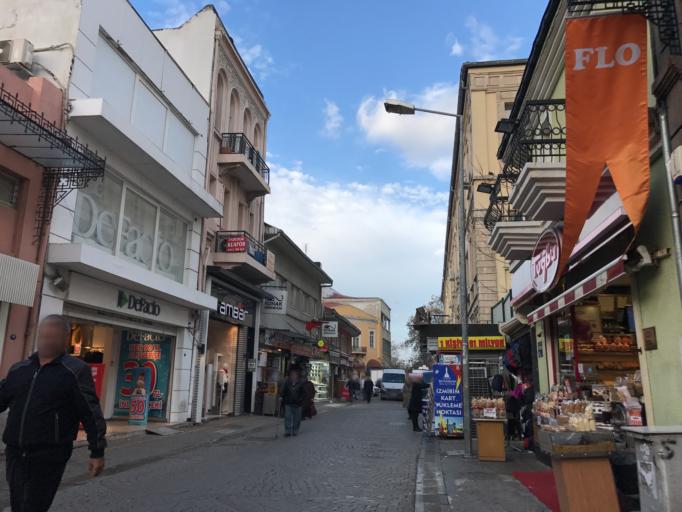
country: TR
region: Izmir
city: Izmir
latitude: 38.4183
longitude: 27.1305
